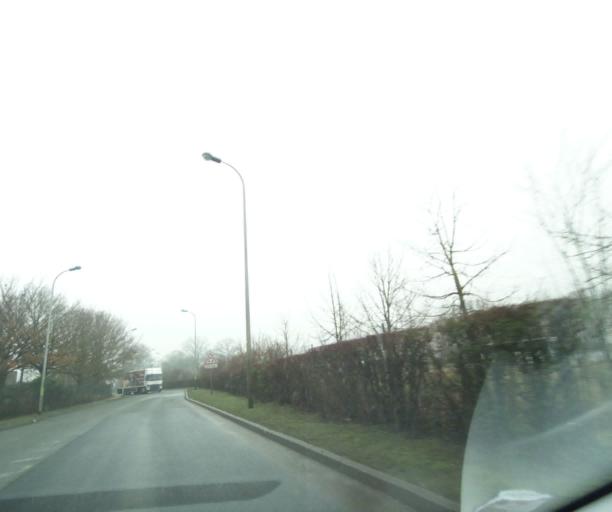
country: FR
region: Ile-de-France
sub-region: Departement de Seine-et-Marne
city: Dammartin-en-Goele
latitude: 49.0638
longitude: 2.6996
